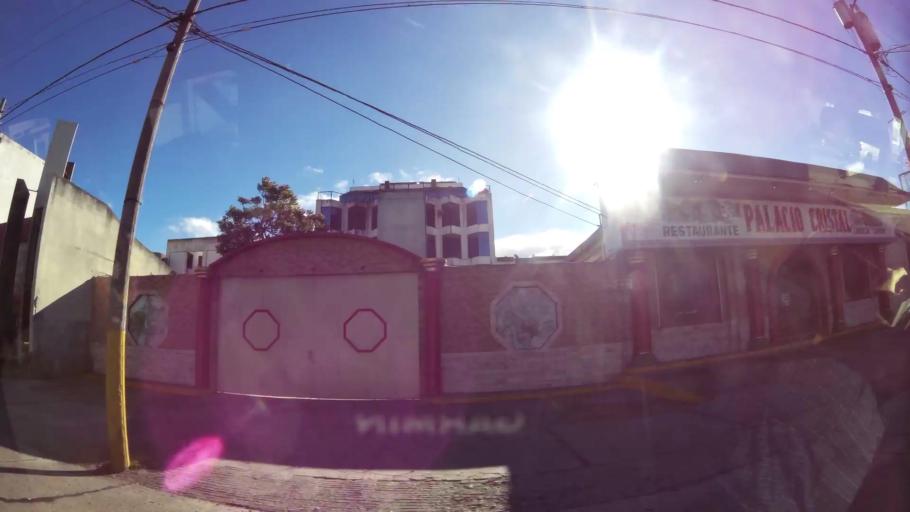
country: GT
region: Guatemala
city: Santa Catarina Pinula
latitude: 14.5996
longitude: -90.5209
